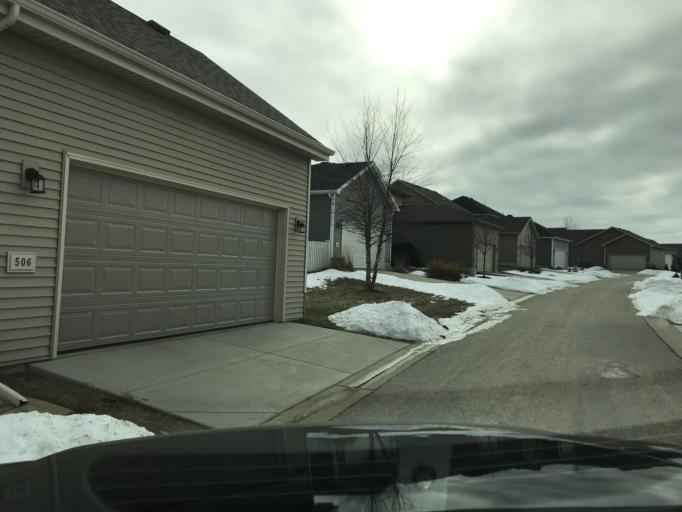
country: US
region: Wisconsin
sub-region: Dane County
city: Monona
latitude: 43.0911
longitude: -89.2735
